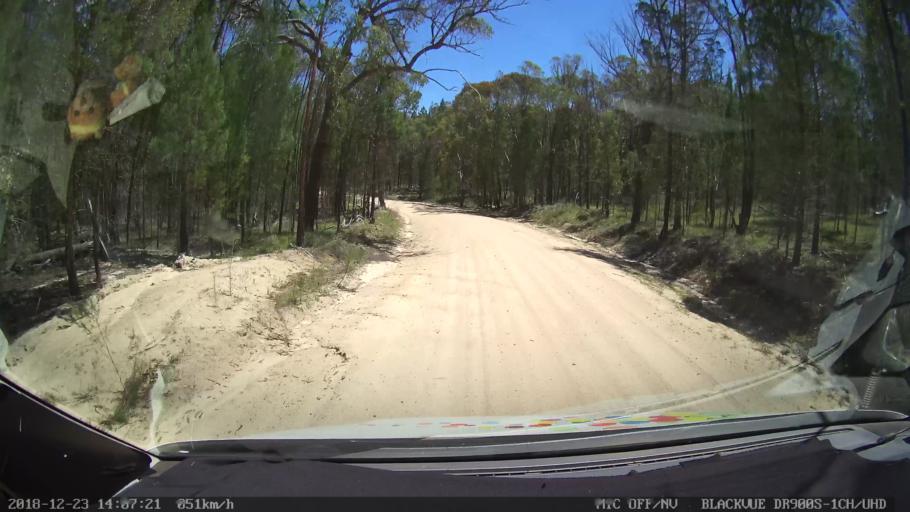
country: AU
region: New South Wales
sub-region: Tamworth Municipality
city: Manilla
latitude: -30.6353
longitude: 151.0720
